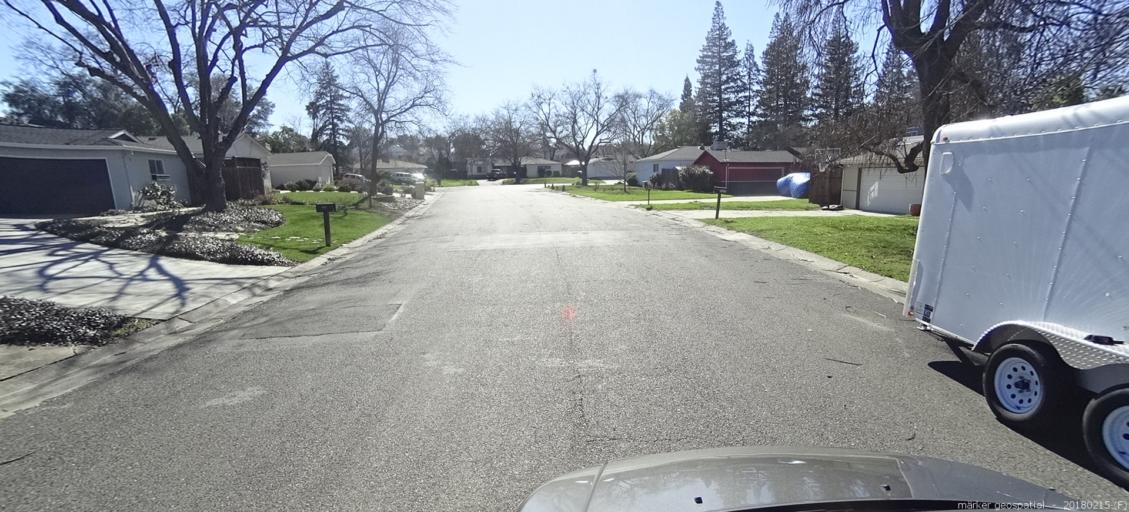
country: US
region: California
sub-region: Sacramento County
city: Fair Oaks
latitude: 38.6649
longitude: -121.3049
